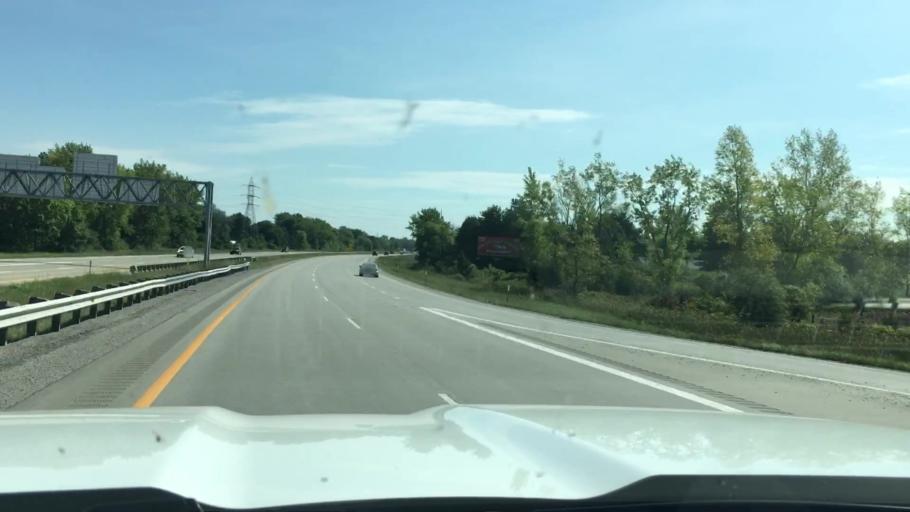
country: US
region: Michigan
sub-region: Bay County
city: Bay City
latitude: 43.5963
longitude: -83.9445
